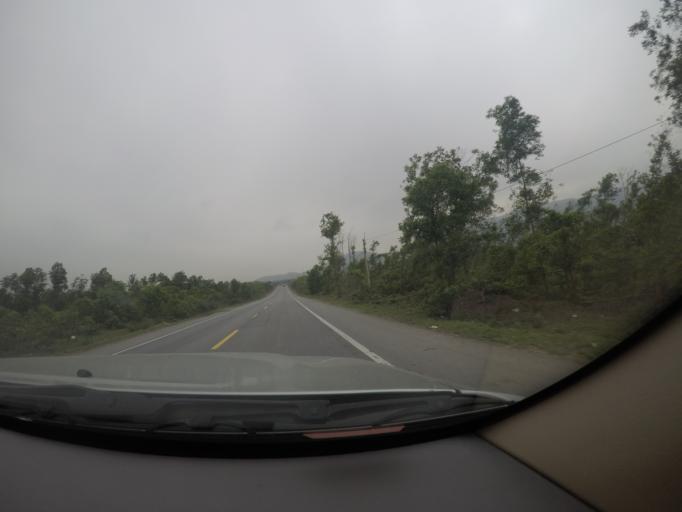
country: VN
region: Ha Tinh
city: Ky Anh
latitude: 18.0305
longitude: 106.3237
